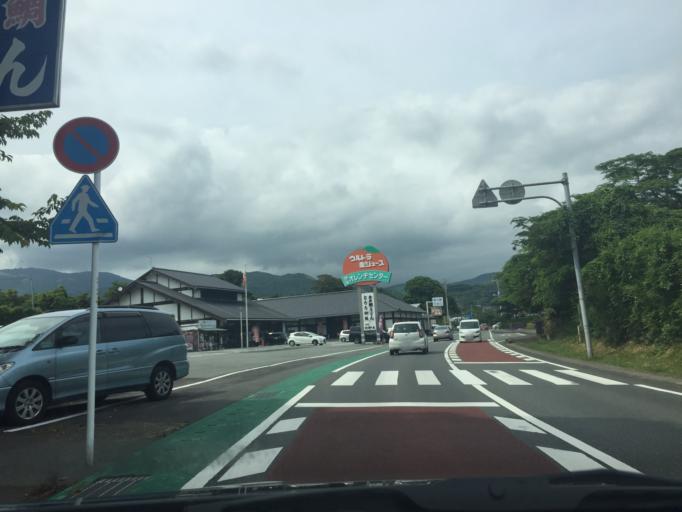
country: JP
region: Shizuoka
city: Shimoda
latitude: 34.7586
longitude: 139.0194
